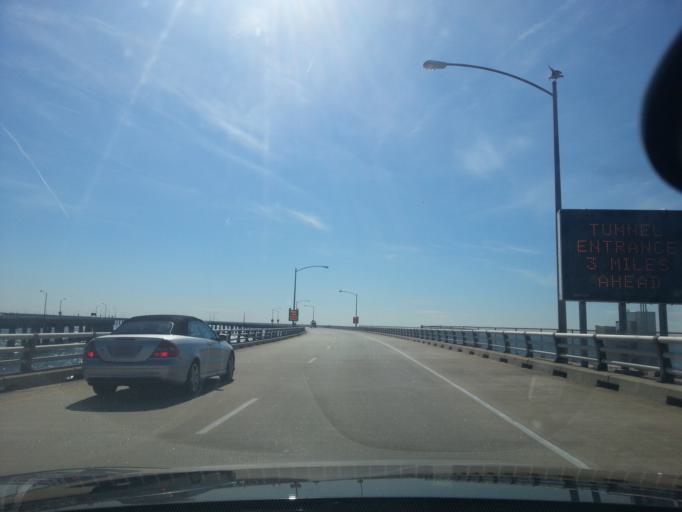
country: US
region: Virginia
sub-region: City of Virginia Beach
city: Virginia Beach
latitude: 37.0328
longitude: -76.0831
